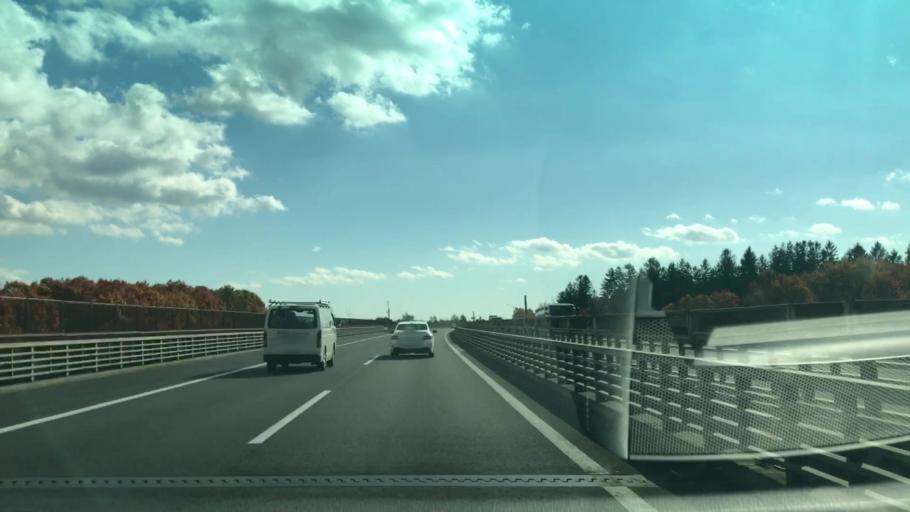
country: JP
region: Hokkaido
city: Kitahiroshima
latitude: 42.9144
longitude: 141.5484
